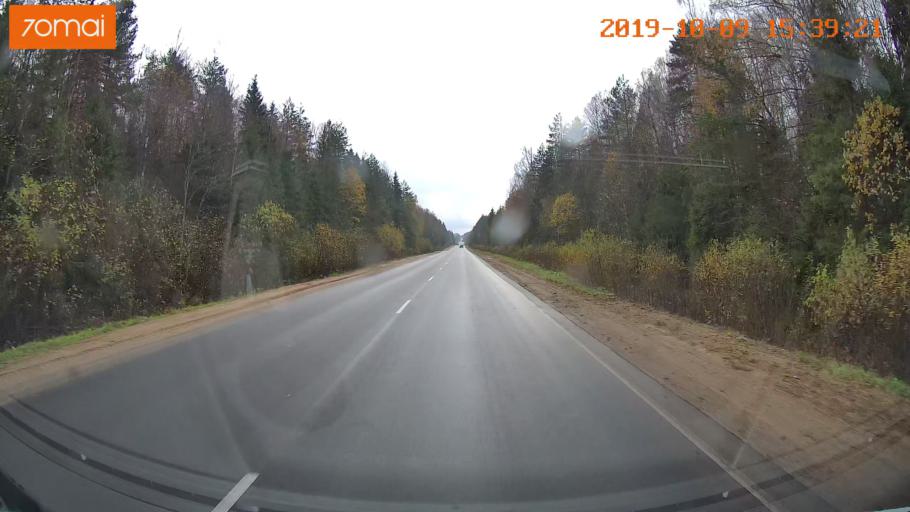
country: RU
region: Kostroma
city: Oktyabr'skiy
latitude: 57.8979
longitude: 41.1663
